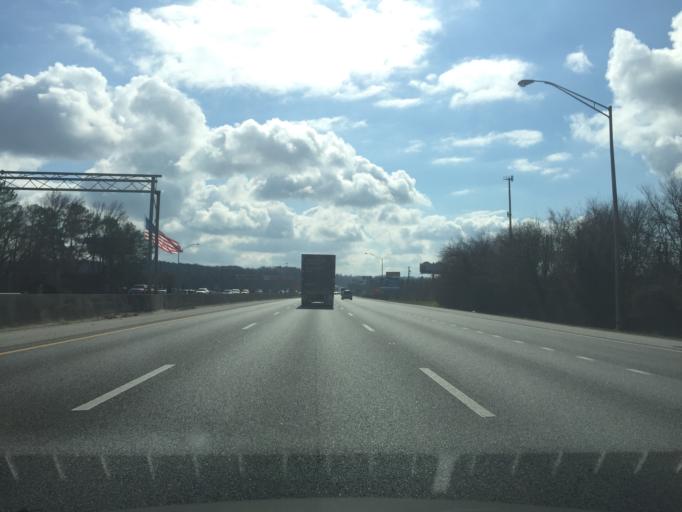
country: US
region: Georgia
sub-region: Catoosa County
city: Indian Springs
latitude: 34.9874
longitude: -85.2024
